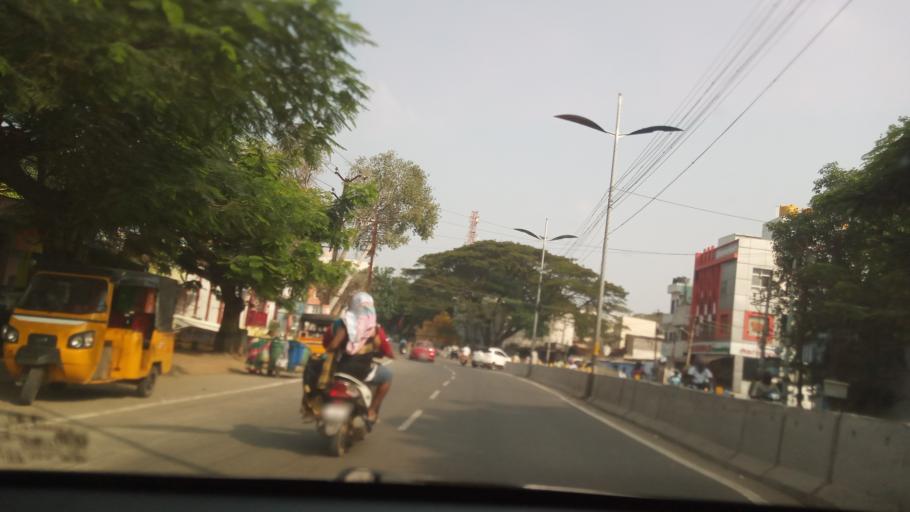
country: IN
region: Tamil Nadu
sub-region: Coimbatore
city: Coimbatore
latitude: 11.0022
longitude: 76.9483
